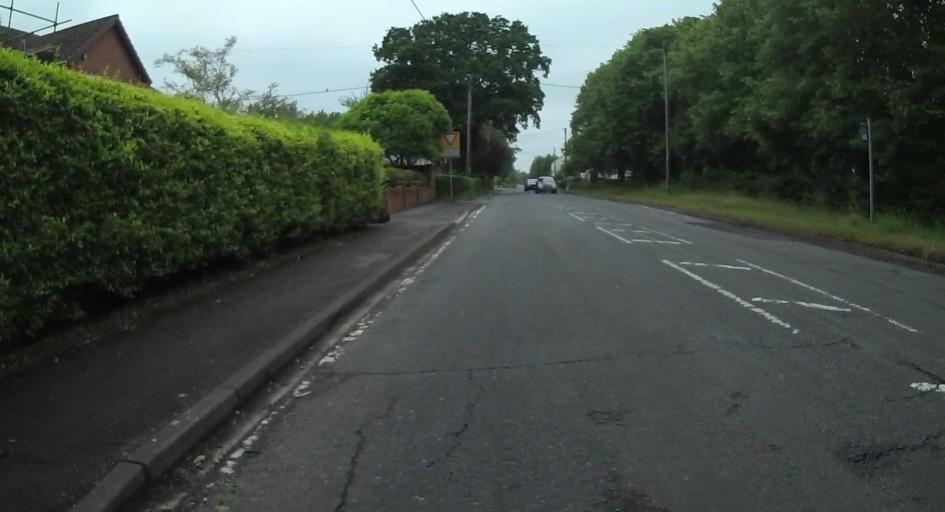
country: GB
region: England
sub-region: Wokingham
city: Swallowfield
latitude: 51.3619
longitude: -0.9634
